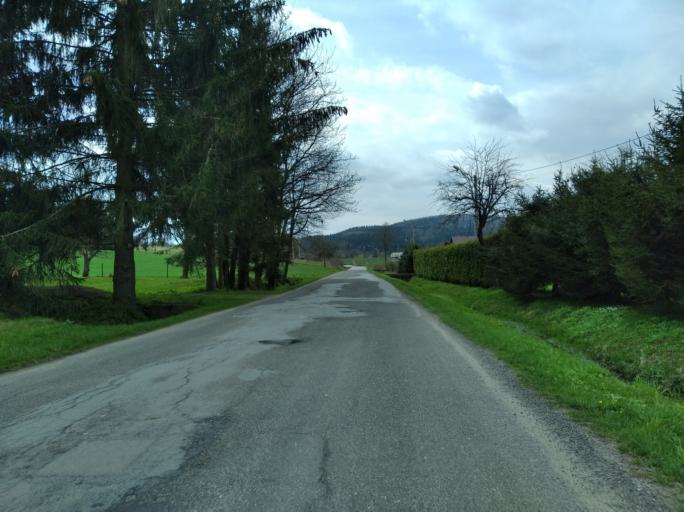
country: PL
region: Subcarpathian Voivodeship
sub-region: Powiat strzyzowski
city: Wysoka Strzyzowska
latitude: 49.8516
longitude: 21.7013
